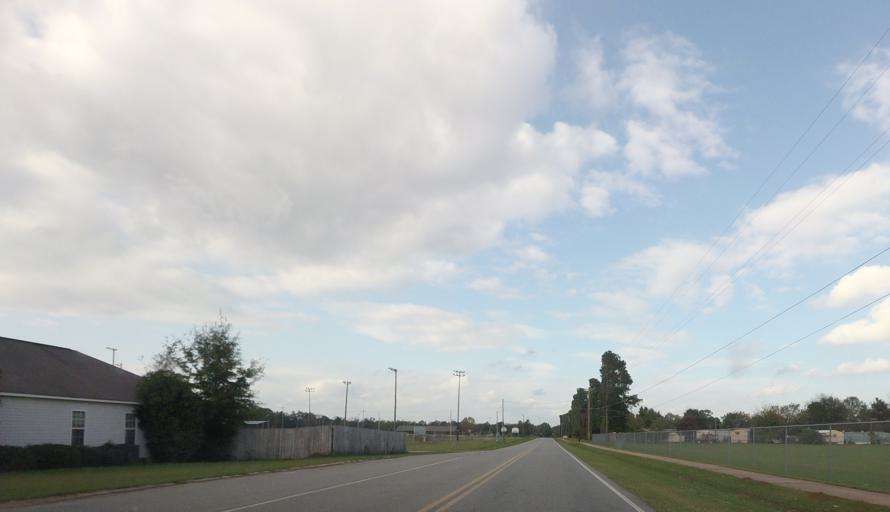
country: US
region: Georgia
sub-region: Houston County
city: Centerville
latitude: 32.6374
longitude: -83.6455
